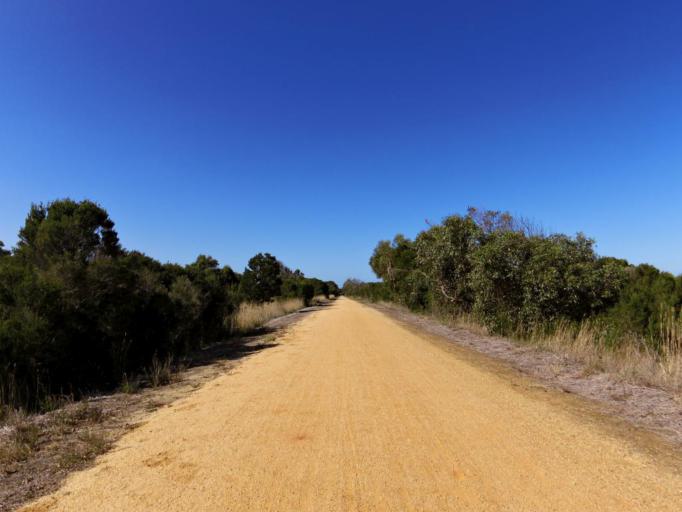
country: AU
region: Victoria
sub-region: Bass Coast
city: North Wonthaggi
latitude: -38.5832
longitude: 145.5544
